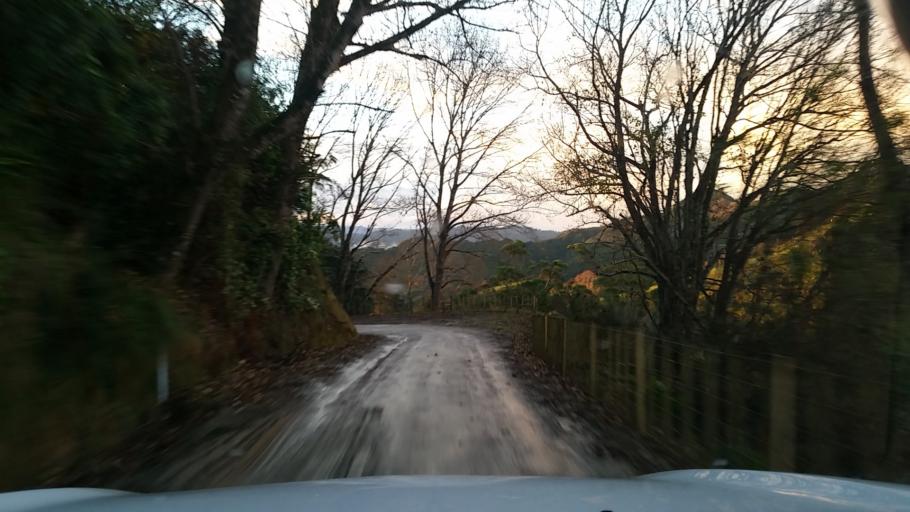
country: NZ
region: Manawatu-Wanganui
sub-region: Wanganui District
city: Wanganui
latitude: -39.7695
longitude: 174.8719
